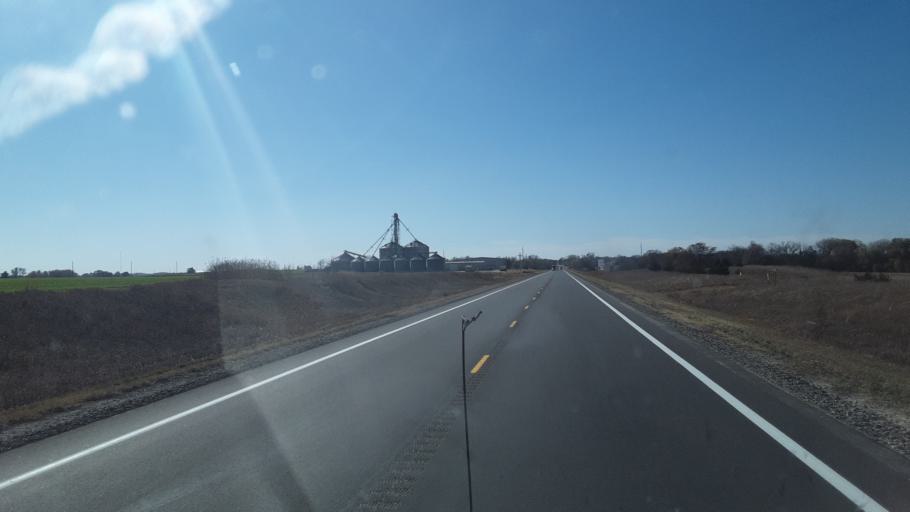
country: US
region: Kansas
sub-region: Rice County
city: Lyons
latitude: 38.3597
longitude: -98.1706
